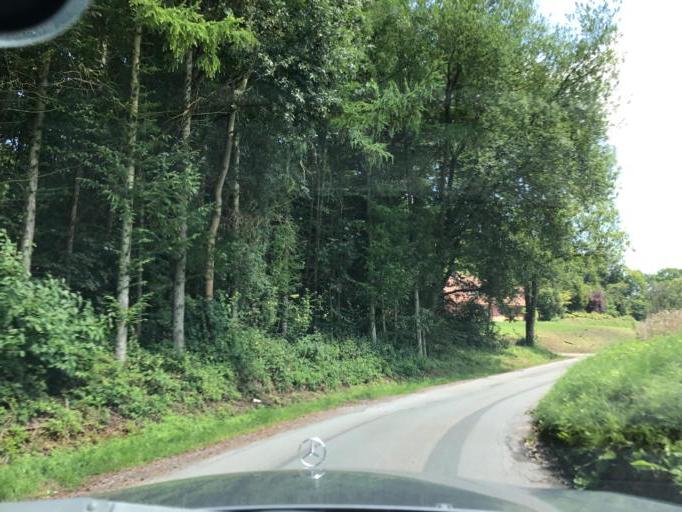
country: DE
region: Lower Saxony
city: Hagen
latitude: 52.2028
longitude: 7.9527
